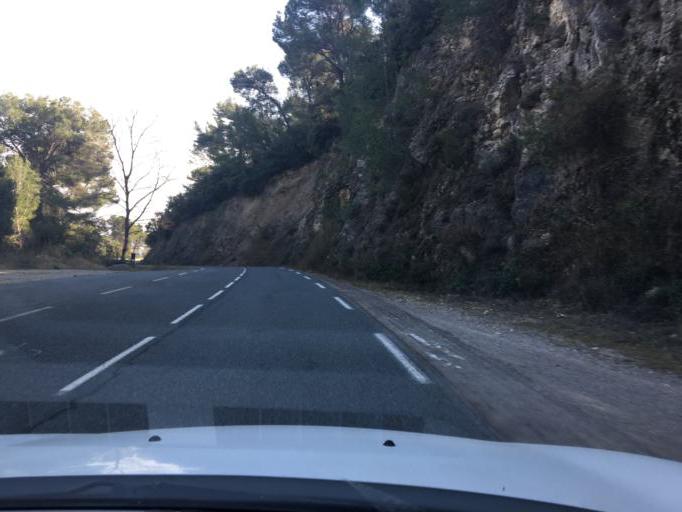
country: FR
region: Provence-Alpes-Cote d'Azur
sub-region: Departement du Var
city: Callas
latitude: 43.6026
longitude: 6.5497
